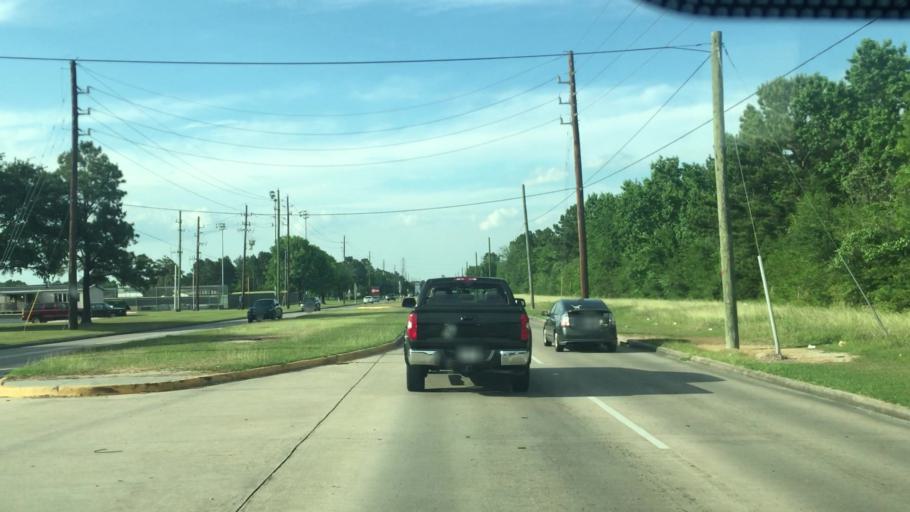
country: US
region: Texas
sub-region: Harris County
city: Hudson
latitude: 29.9650
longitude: -95.4975
